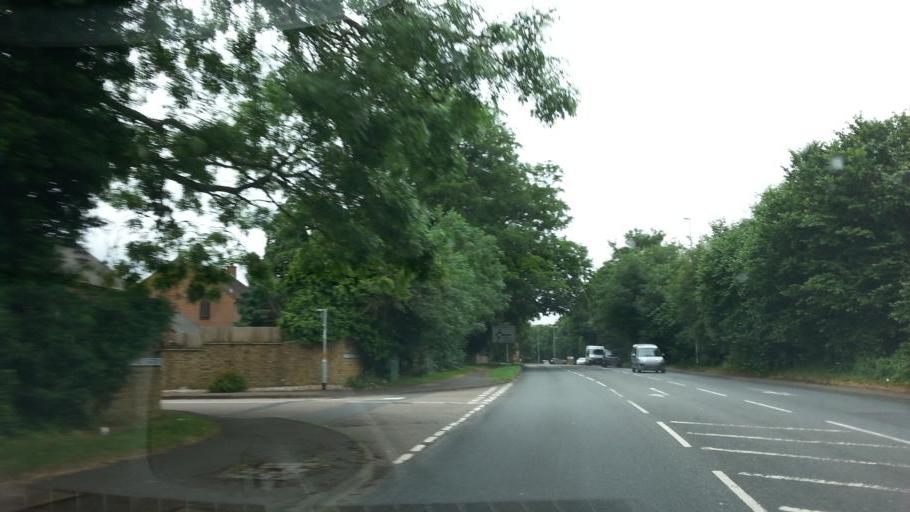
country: GB
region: England
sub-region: Northamptonshire
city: Northampton
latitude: 52.2607
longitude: -0.8218
